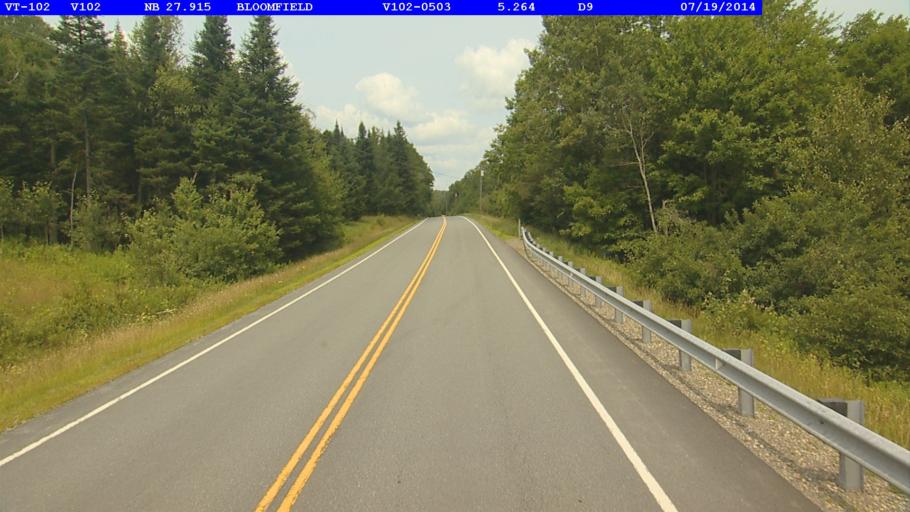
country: US
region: New Hampshire
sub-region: Coos County
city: Colebrook
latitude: 44.8064
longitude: -71.5737
